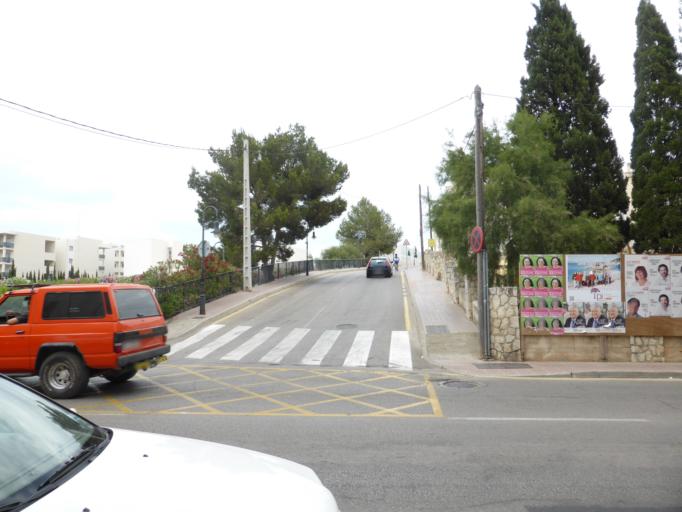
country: ES
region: Balearic Islands
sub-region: Illes Balears
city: Port d'Alcudia
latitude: 39.8422
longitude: 3.1350
